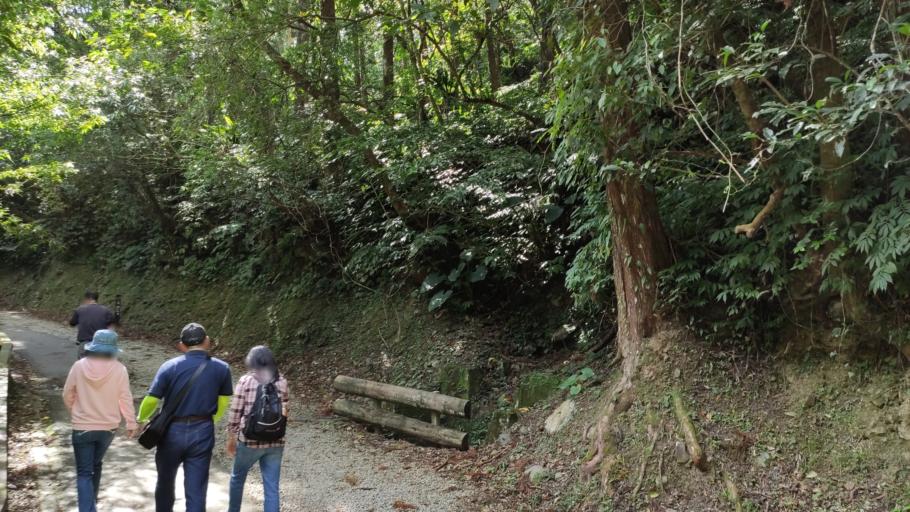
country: TW
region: Taiwan
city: Daxi
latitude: 24.8243
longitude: 121.4494
